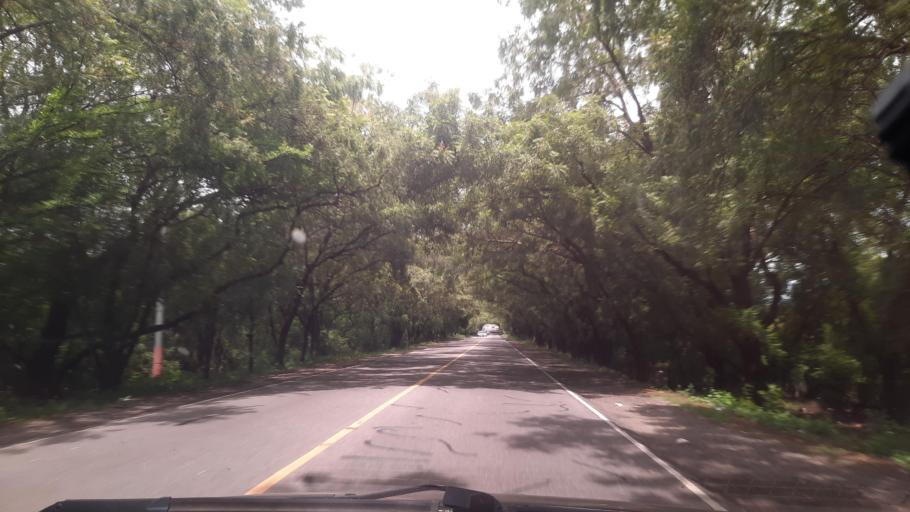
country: GT
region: Zacapa
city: Estanzuela
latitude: 15.0190
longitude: -89.5796
